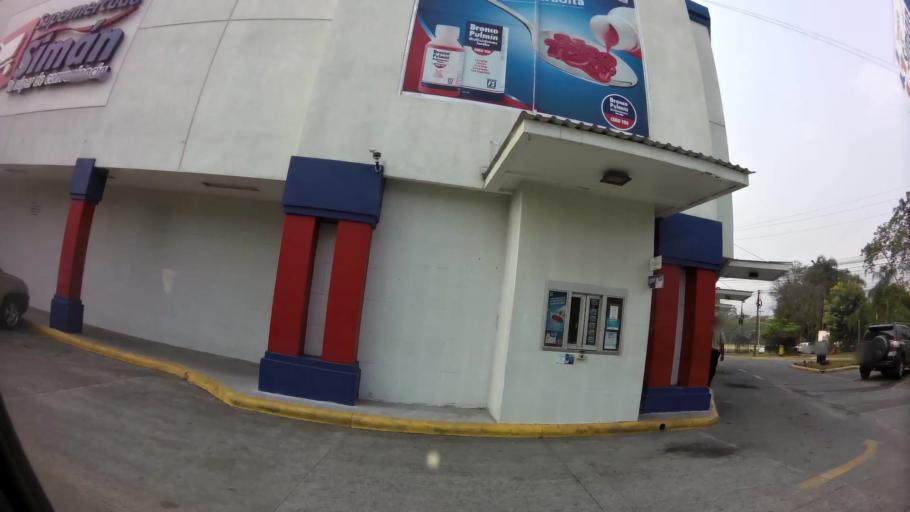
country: HN
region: Cortes
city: El Zapotal del Norte
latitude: 15.5241
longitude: -88.0367
